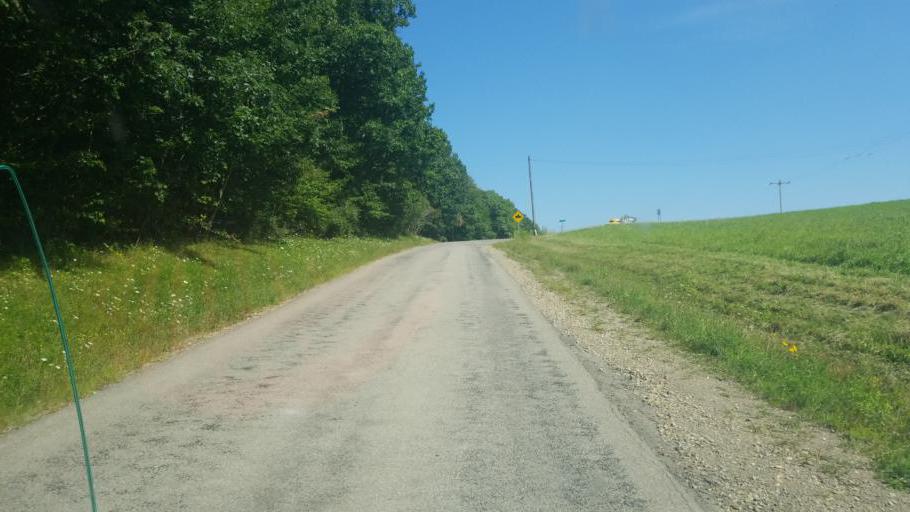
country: US
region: New York
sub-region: Allegany County
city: Bolivar
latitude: 42.0659
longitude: -78.0550
